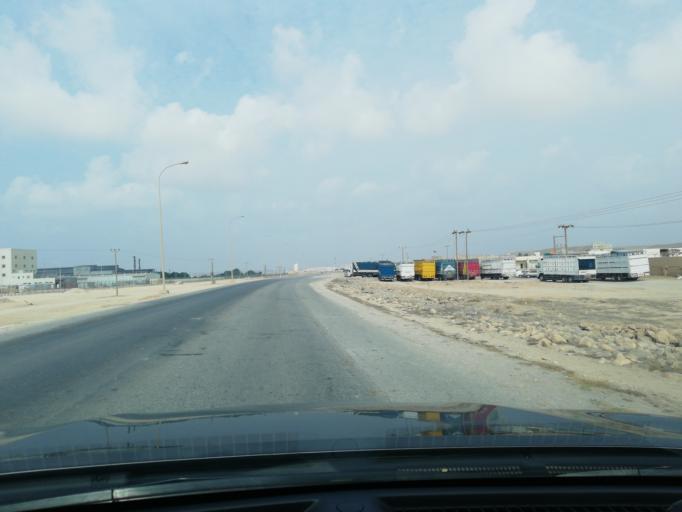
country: OM
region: Zufar
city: Salalah
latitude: 16.9494
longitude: 53.9790
